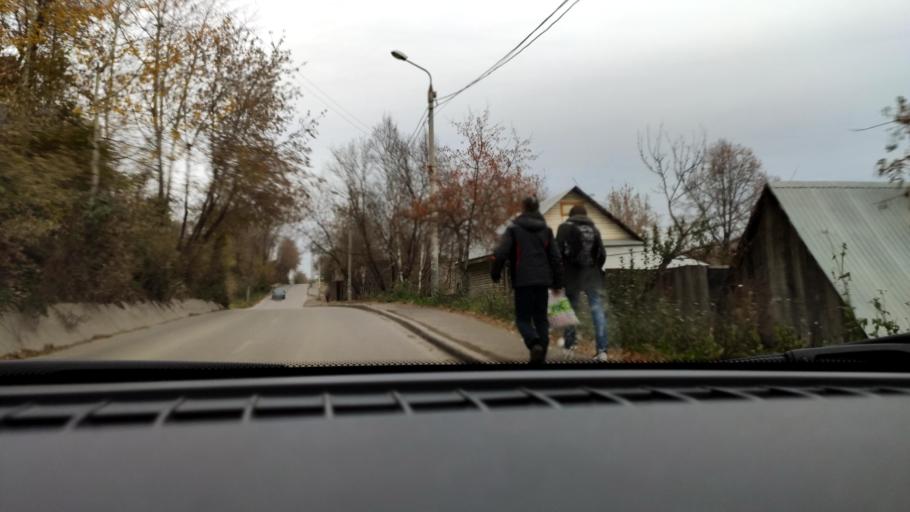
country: RU
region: Perm
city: Perm
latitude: 58.0305
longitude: 56.3136
